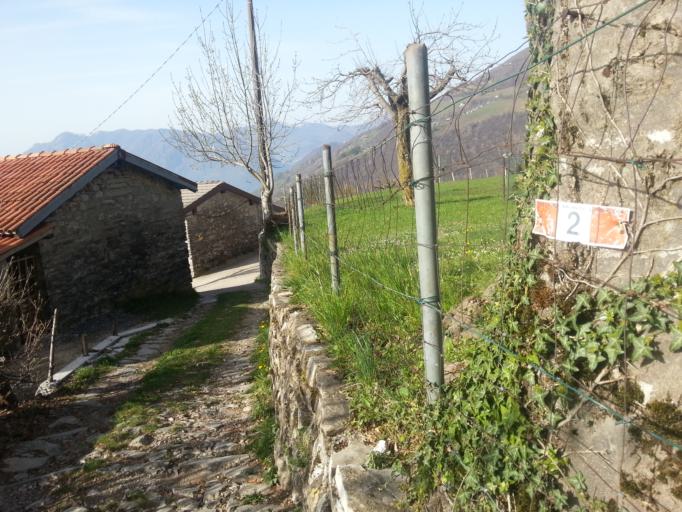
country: IT
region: Lombardy
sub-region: Provincia di Como
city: Lenno
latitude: 45.9851
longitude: 9.1815
